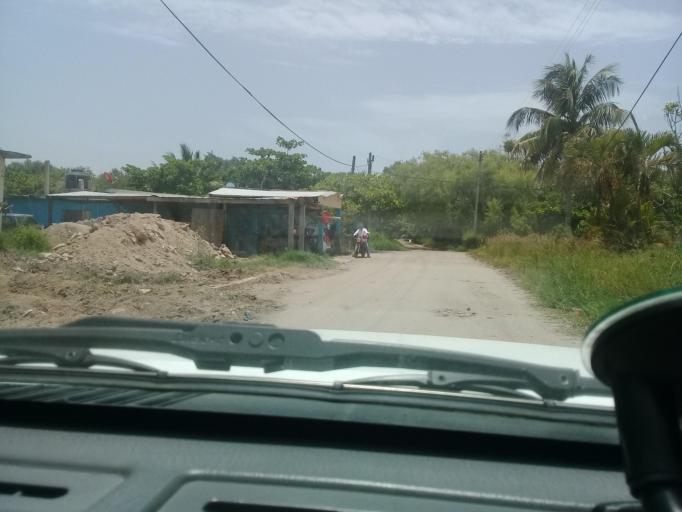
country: MX
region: Veracruz
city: Anahuac
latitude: 22.2261
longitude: -97.8185
